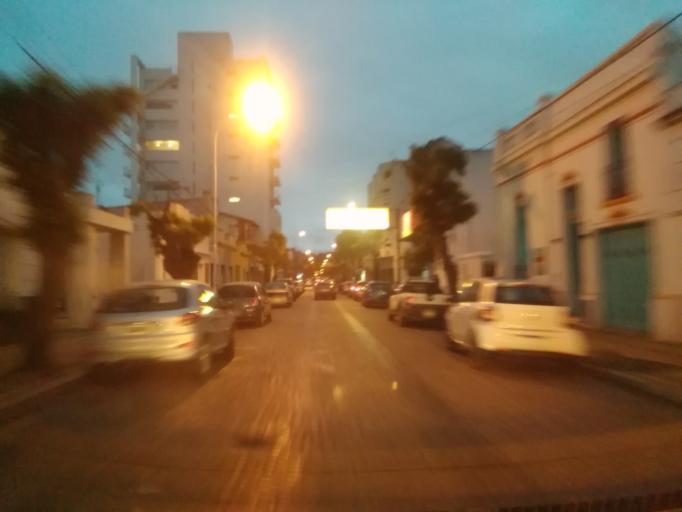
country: AR
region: Buenos Aires
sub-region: Partido de Tandil
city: Tandil
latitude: -37.3249
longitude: -59.1406
